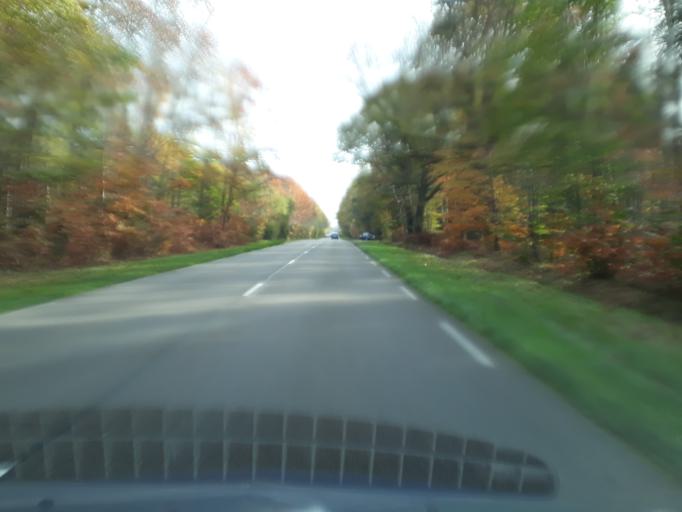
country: FR
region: Ile-de-France
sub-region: Departement de Seine-et-Marne
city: Champagne-sur-Seine
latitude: 48.4199
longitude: 2.8128
